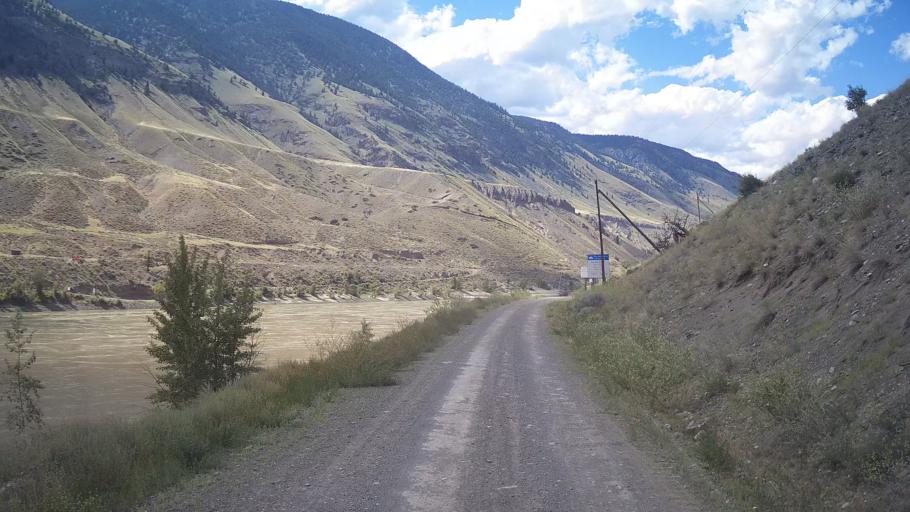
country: CA
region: British Columbia
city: Lillooet
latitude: 51.1828
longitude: -122.1294
